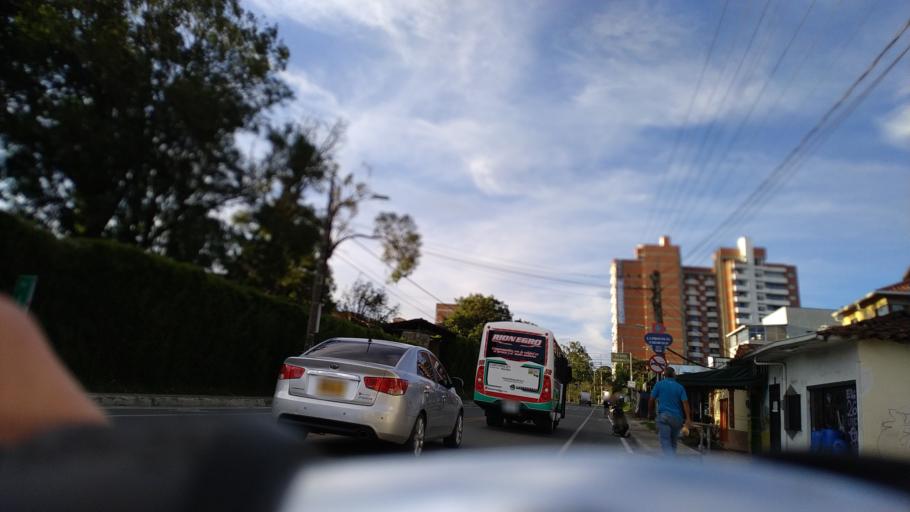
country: CO
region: Antioquia
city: Rionegro
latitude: 6.1310
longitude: -75.3795
